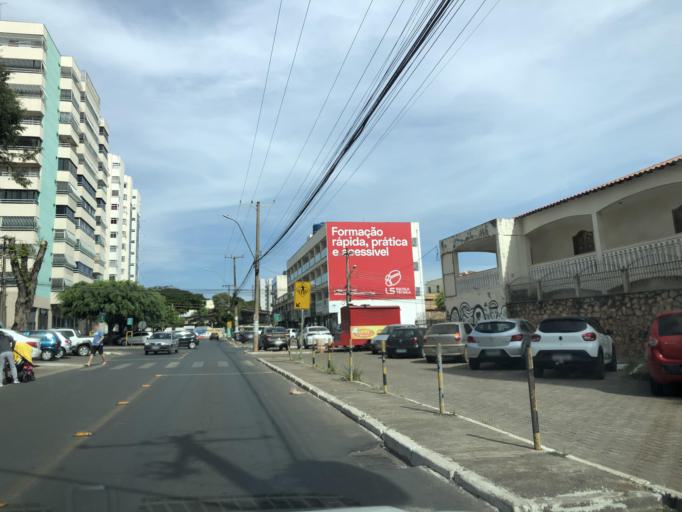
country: BR
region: Federal District
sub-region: Brasilia
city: Brasilia
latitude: -15.8305
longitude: -48.0595
